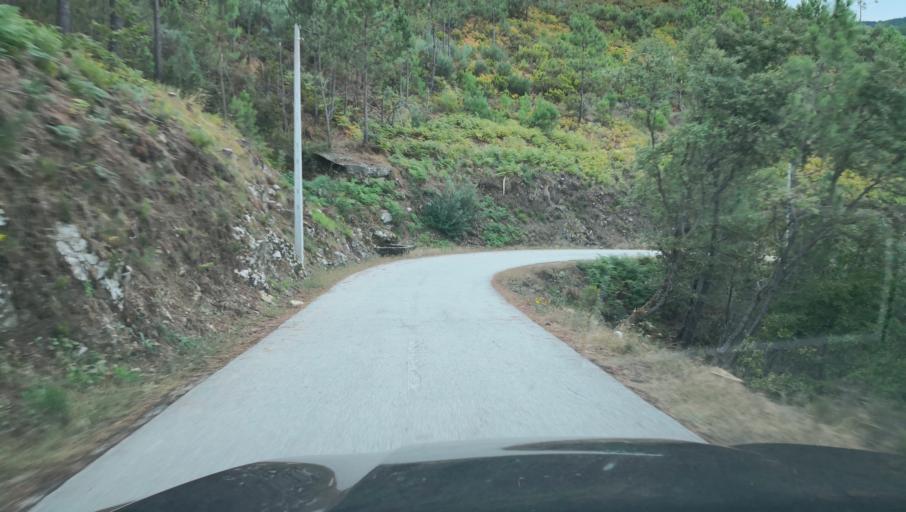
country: PT
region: Vila Real
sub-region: Santa Marta de Penaguiao
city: Santa Marta de Penaguiao
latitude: 41.2613
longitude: -7.8647
